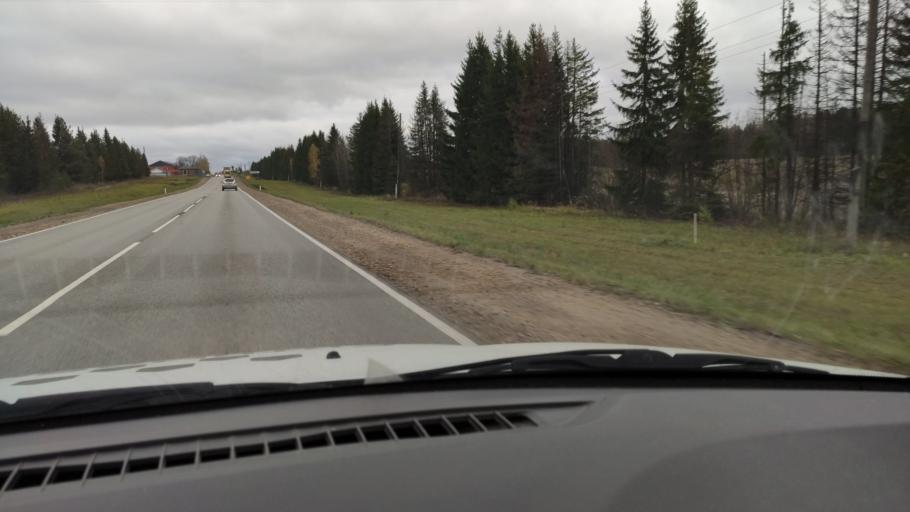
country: RU
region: Kirov
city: Slobodskoy
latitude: 58.7449
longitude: 50.3046
